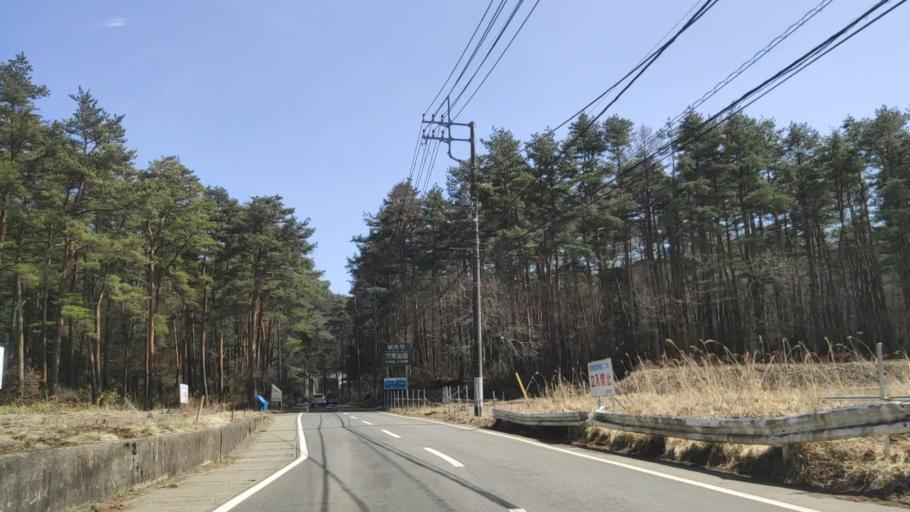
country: JP
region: Yamanashi
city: Fujikawaguchiko
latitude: 35.4646
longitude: 138.8139
